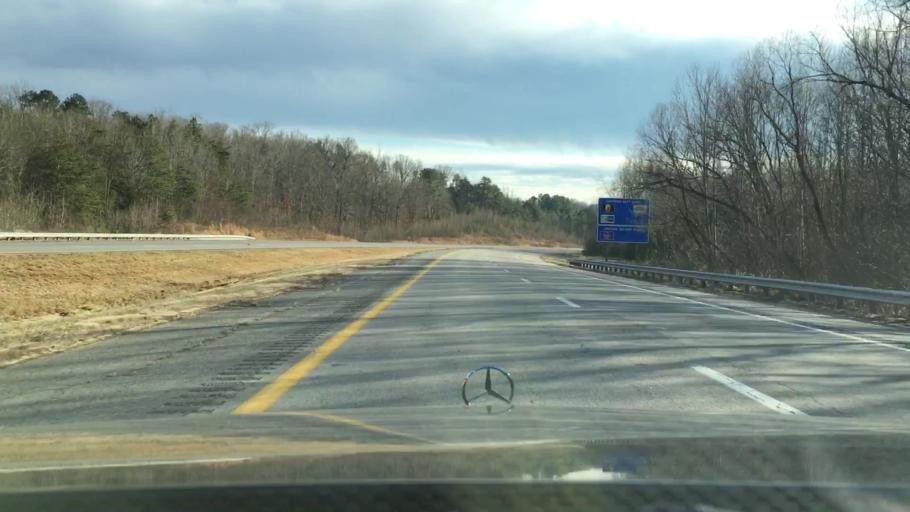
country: US
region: Virginia
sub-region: City of Danville
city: Danville
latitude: 36.6049
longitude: -79.3573
